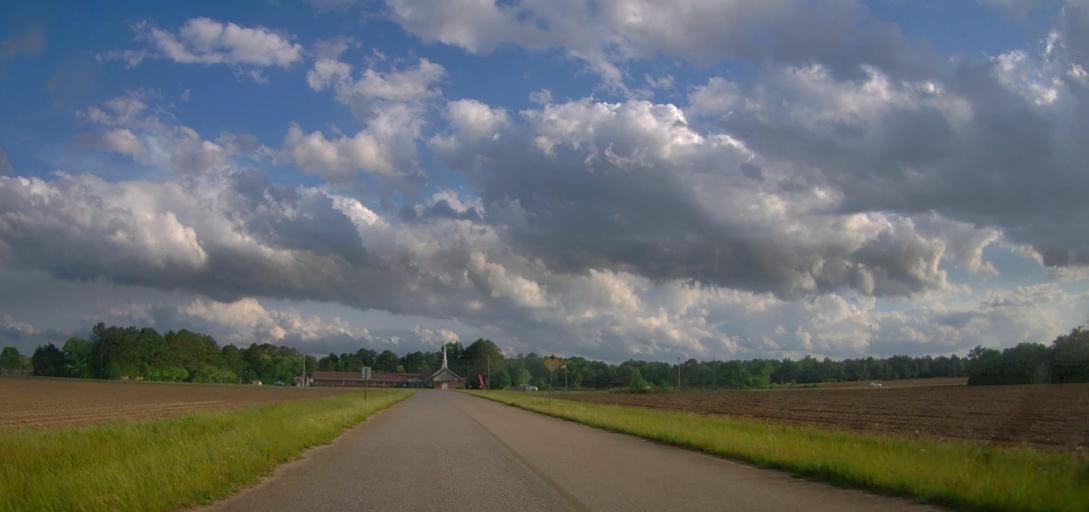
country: US
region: Georgia
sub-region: Peach County
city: Byron
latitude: 32.6079
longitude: -83.7736
